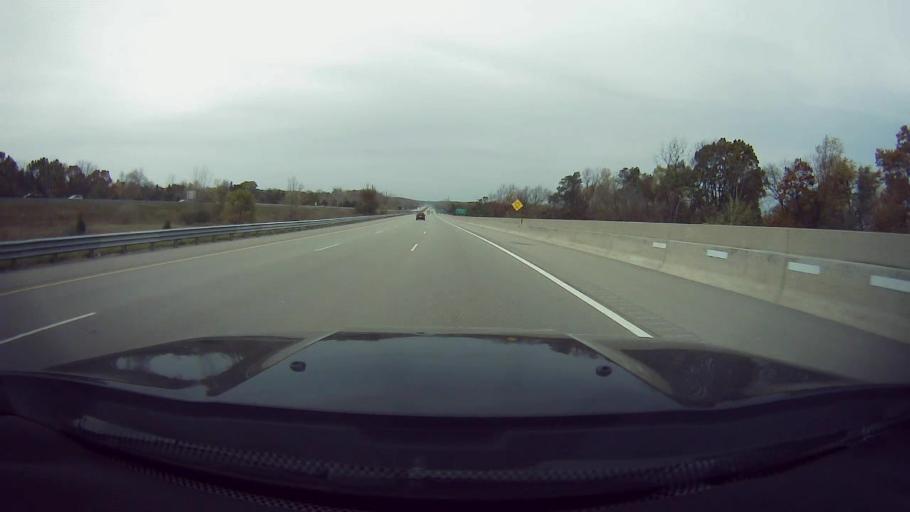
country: US
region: Michigan
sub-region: Oakland County
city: Clarkston
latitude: 42.7455
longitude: -83.3962
